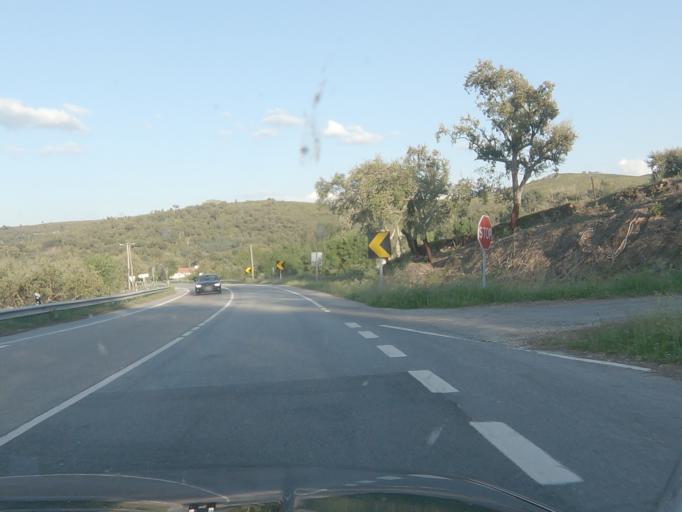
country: PT
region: Portalegre
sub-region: Portalegre
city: Sao Juliao
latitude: 39.3639
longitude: -7.3334
